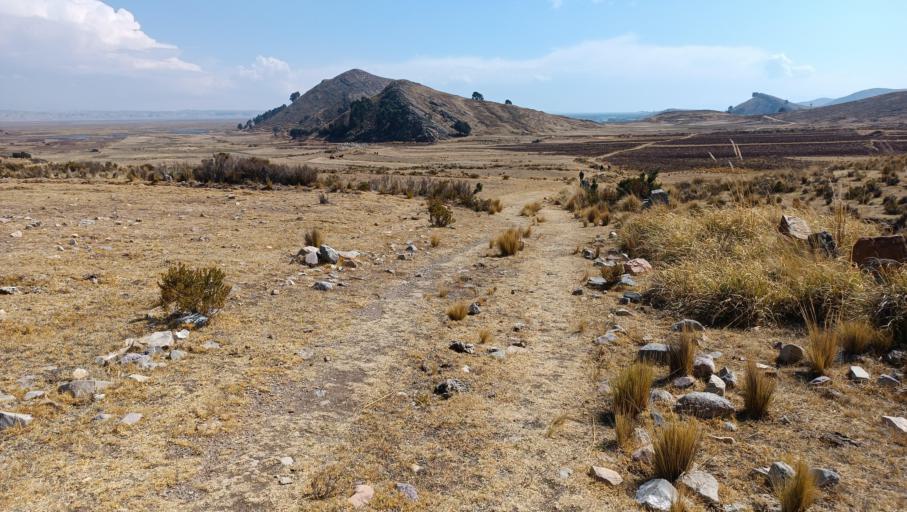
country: BO
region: La Paz
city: Batallas
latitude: -16.3476
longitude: -68.6609
